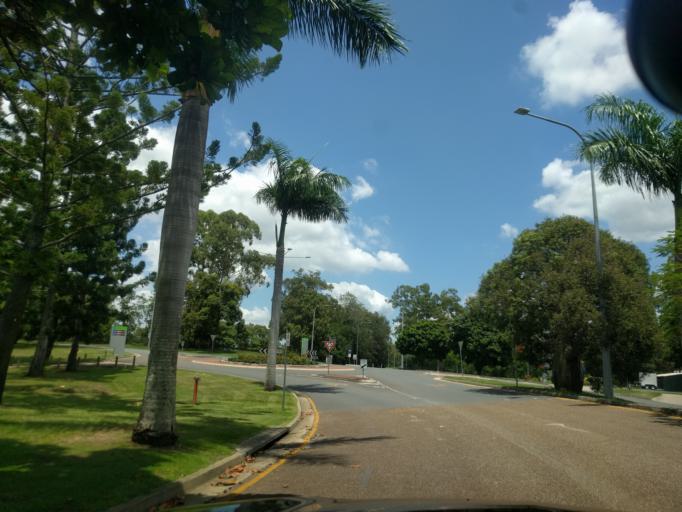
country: AU
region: Queensland
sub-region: Brisbane
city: South Brisbane
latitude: -27.4922
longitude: 153.0127
